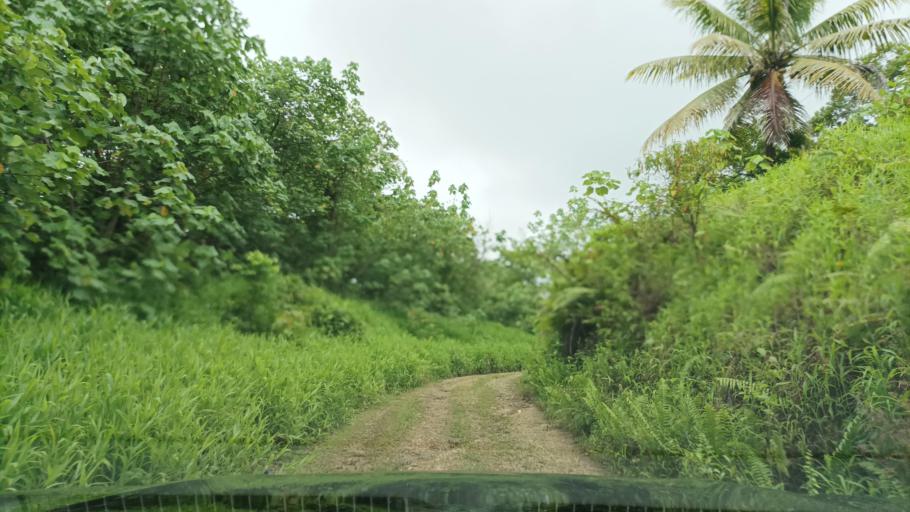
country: FM
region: Pohnpei
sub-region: Madolenihm Municipality
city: Madolenihm Municipality Government
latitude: 6.8241
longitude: 158.2808
